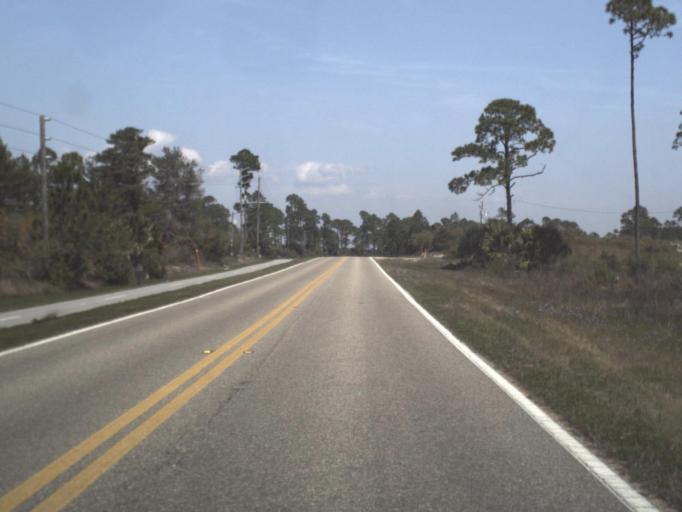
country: US
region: Florida
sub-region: Gulf County
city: Port Saint Joe
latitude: 29.6788
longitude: -85.3404
